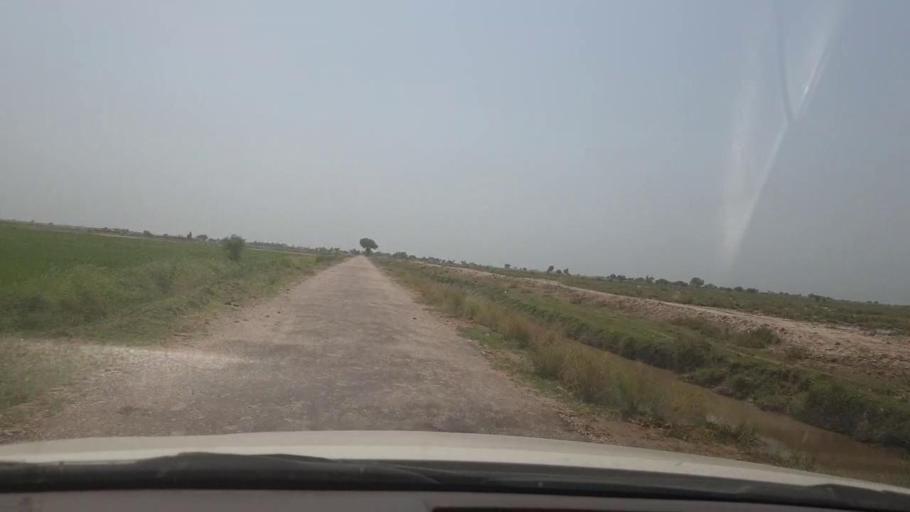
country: PK
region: Sindh
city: Shikarpur
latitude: 28.0459
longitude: 68.5731
